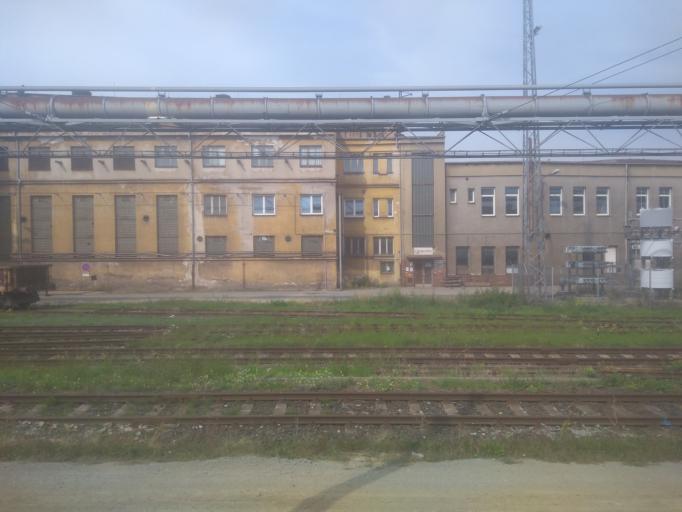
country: CZ
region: Plzensky
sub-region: Okres Plzen-Mesto
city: Pilsen
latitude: 49.7420
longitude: 13.3589
